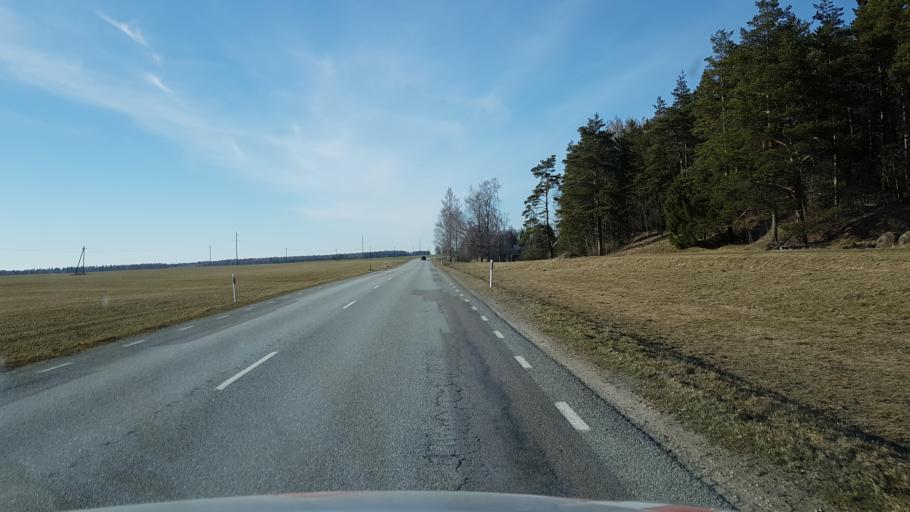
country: EE
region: Laeaene-Virumaa
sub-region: Vinni vald
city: Vinni
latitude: 59.1937
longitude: 26.5676
